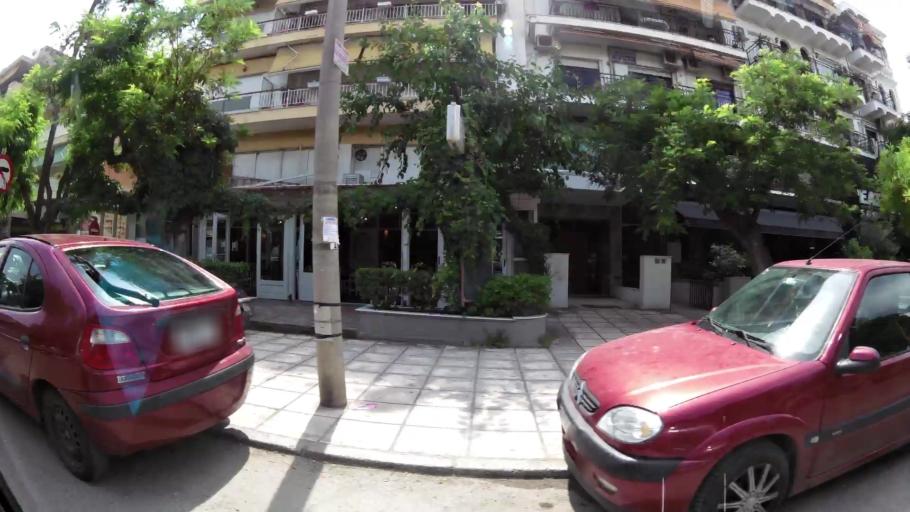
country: GR
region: Central Macedonia
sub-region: Nomos Thessalonikis
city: Pylaia
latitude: 40.6025
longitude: 22.9751
